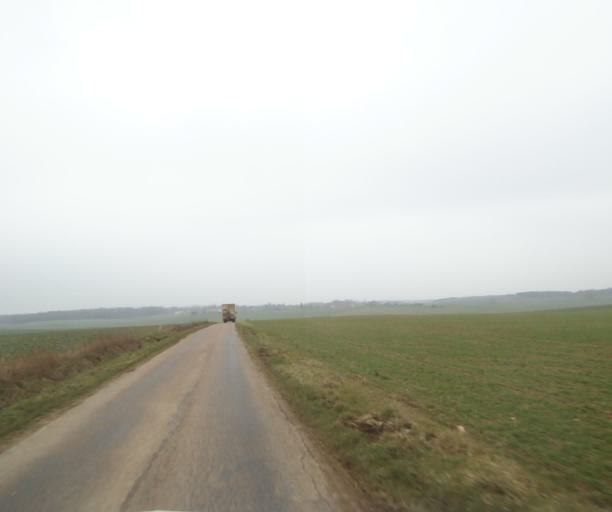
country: FR
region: Champagne-Ardenne
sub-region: Departement de la Haute-Marne
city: Chevillon
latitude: 48.5018
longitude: 5.0805
